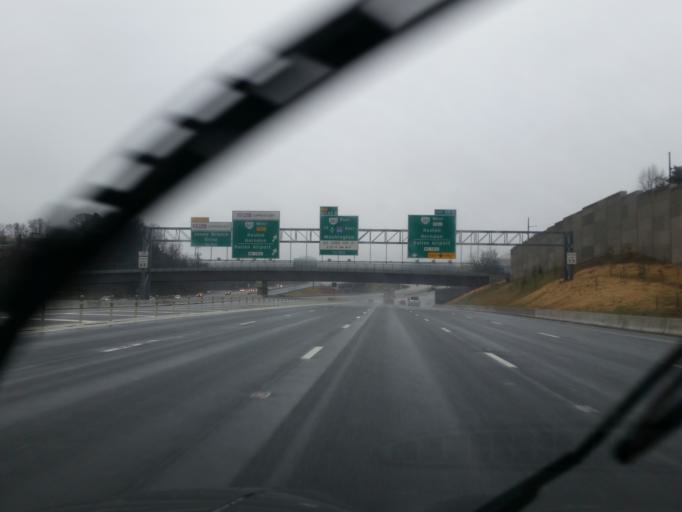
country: US
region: Virginia
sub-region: Fairfax County
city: Pimmit Hills
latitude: 38.9379
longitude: -77.2075
